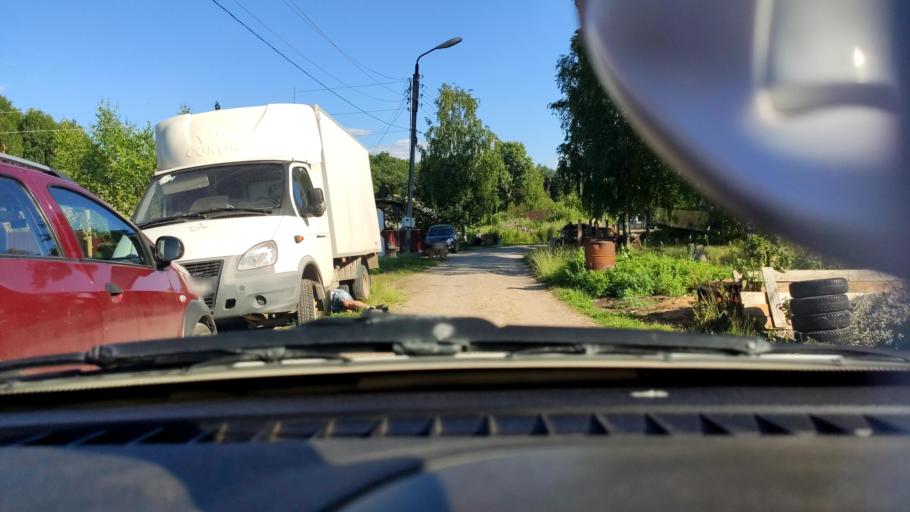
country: RU
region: Perm
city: Overyata
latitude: 58.0803
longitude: 55.8140
